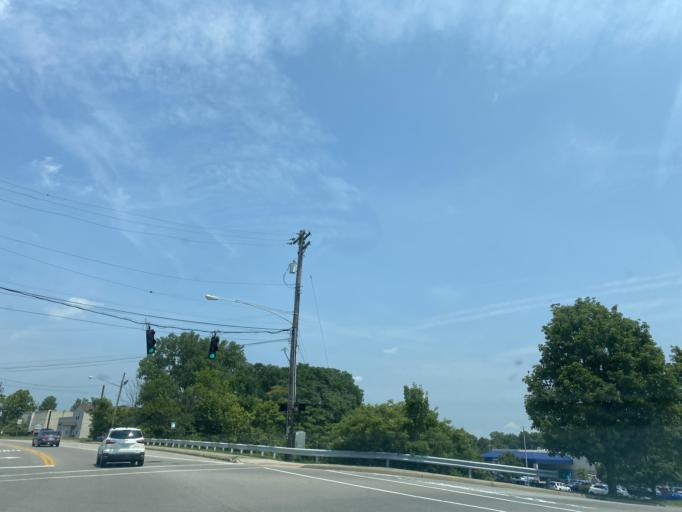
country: US
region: Kentucky
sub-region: Campbell County
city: Highland Heights
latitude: 39.0393
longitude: -84.4495
